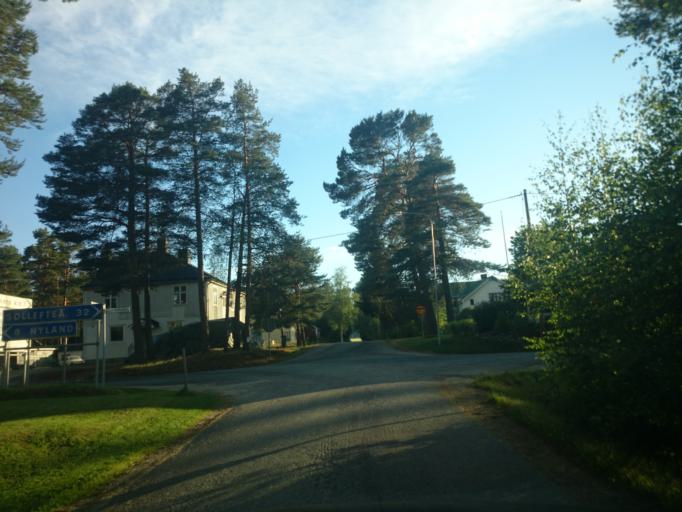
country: SE
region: Vaesternorrland
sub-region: Kramfors Kommun
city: Bollstabruk
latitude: 63.0785
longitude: 17.7533
